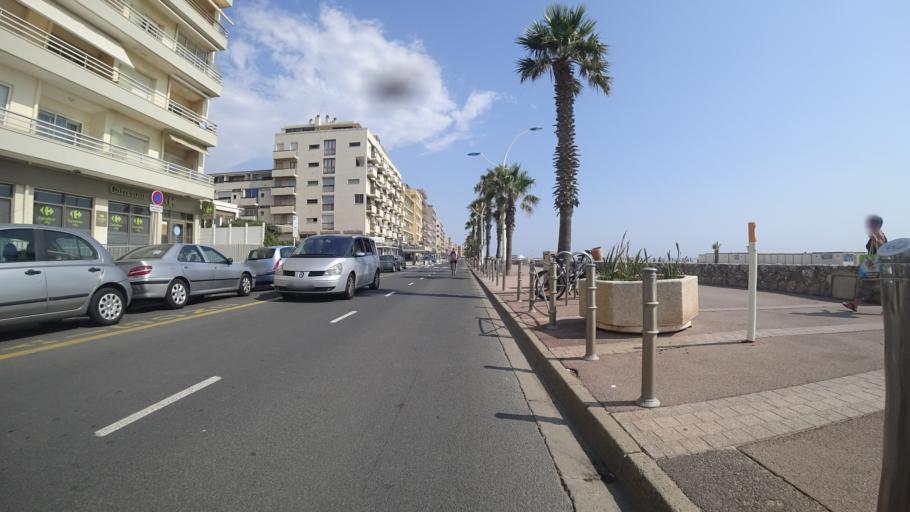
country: FR
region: Languedoc-Roussillon
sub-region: Departement des Pyrenees-Orientales
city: Canet-en-Roussillon
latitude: 42.6940
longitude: 3.0358
